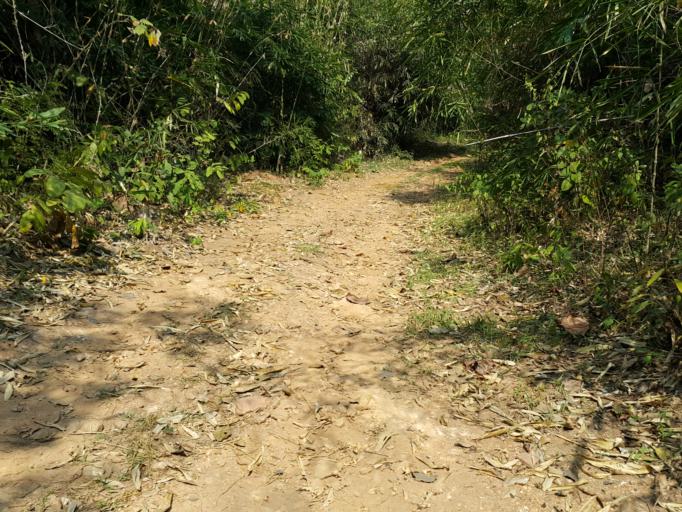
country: TH
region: Sukhothai
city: Thung Saliam
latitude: 17.3235
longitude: 99.4997
